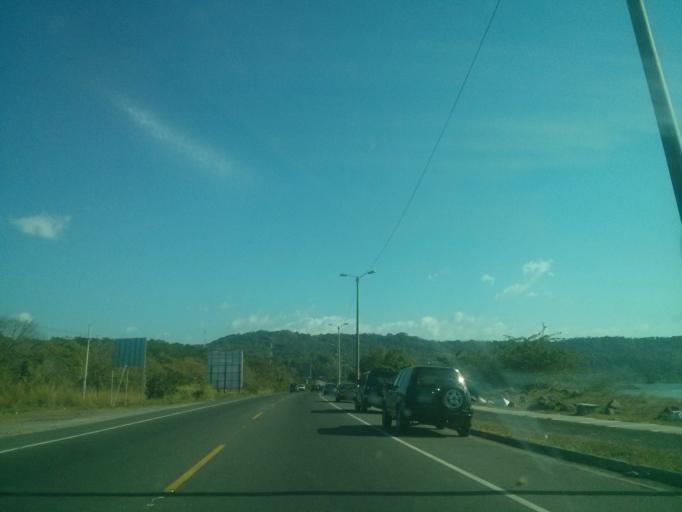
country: CR
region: Puntarenas
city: Esparza
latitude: 9.9266
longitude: -84.7157
